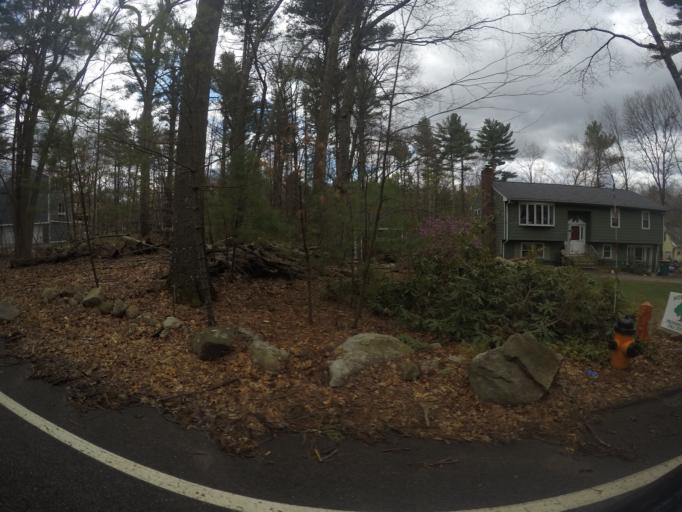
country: US
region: Massachusetts
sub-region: Bristol County
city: Easton
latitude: 42.0519
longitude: -71.1132
